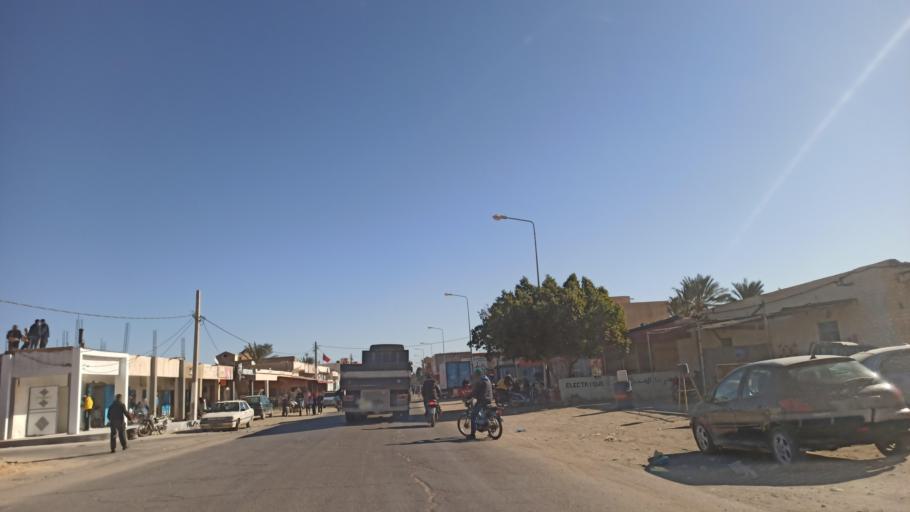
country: TN
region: Gafsa
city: Al Metlaoui
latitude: 34.3162
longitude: 8.3980
